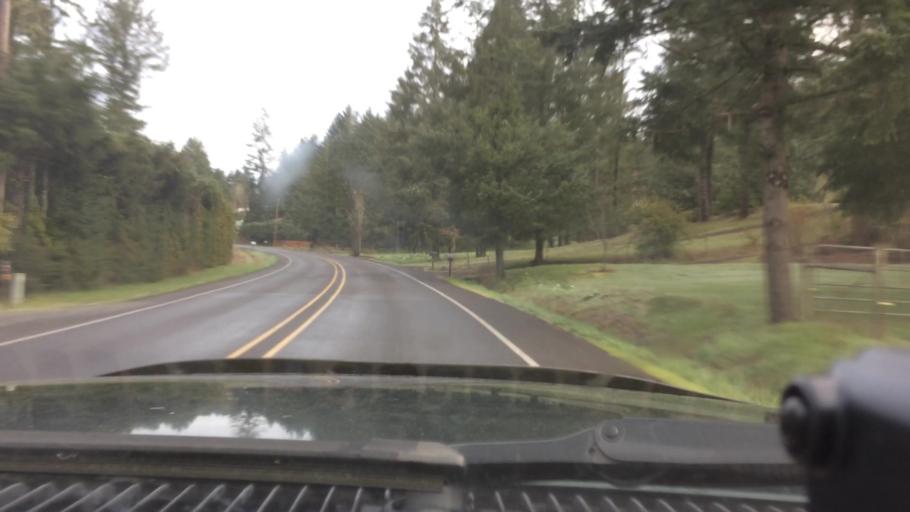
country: US
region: Oregon
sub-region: Lane County
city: Veneta
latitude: 44.1310
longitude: -123.3475
